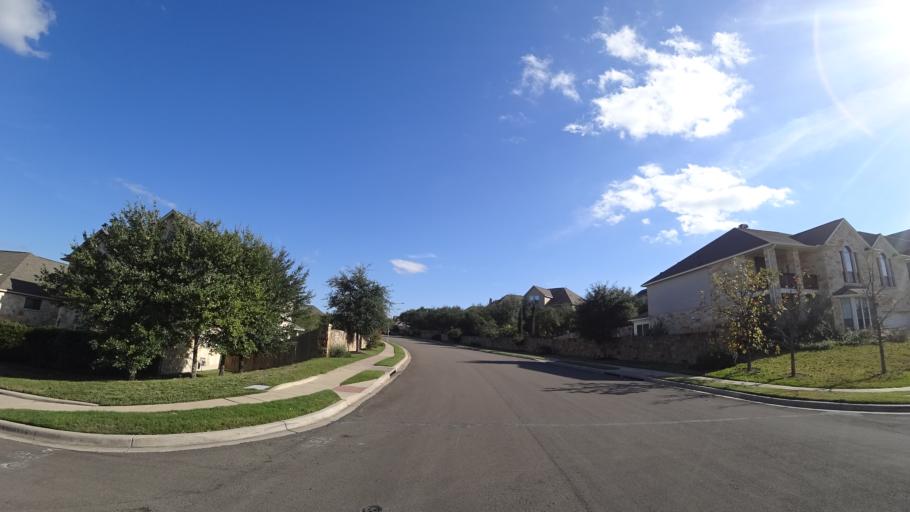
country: US
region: Texas
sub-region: Travis County
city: Barton Creek
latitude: 30.2495
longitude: -97.8773
